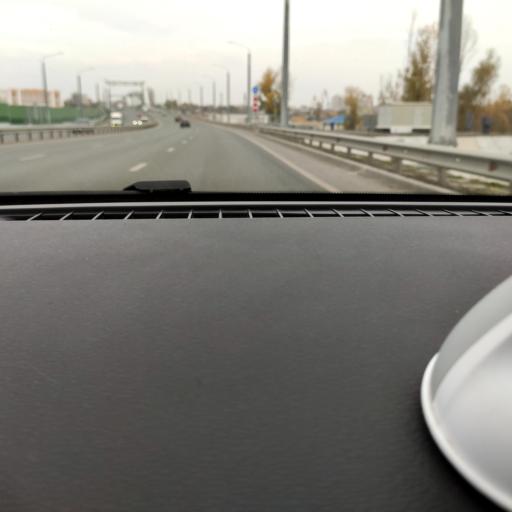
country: RU
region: Samara
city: Samara
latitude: 53.1711
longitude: 50.0861
